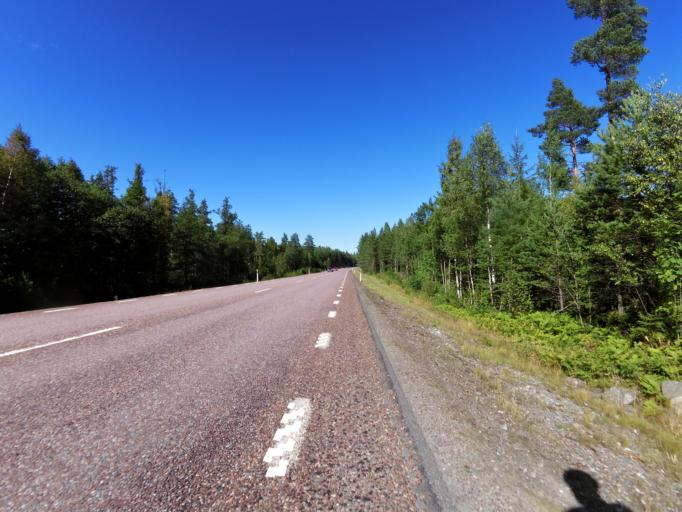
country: SE
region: Gaevleborg
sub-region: Hofors Kommun
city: Hofors
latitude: 60.5519
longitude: 16.4764
